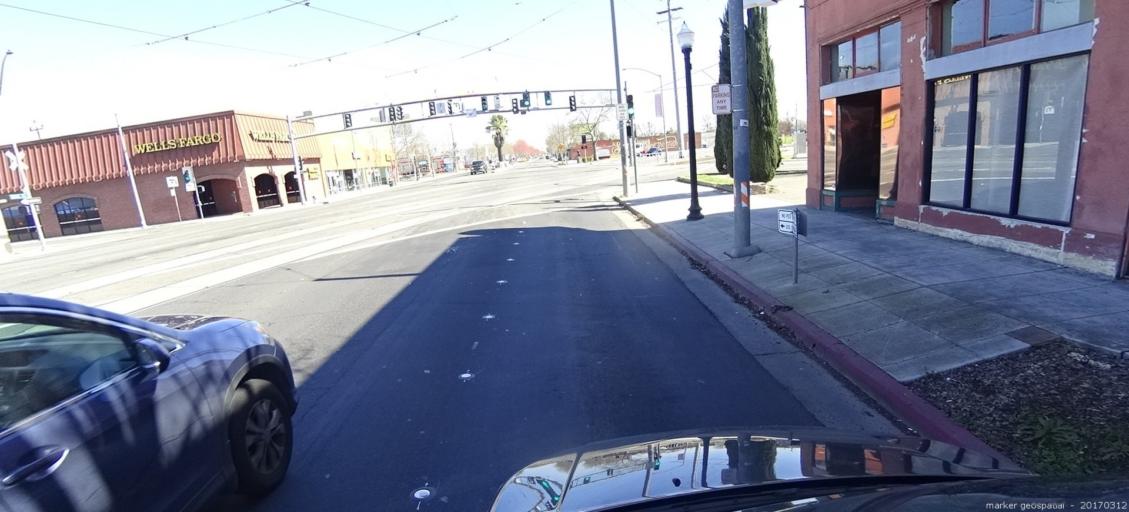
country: US
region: California
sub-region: Sacramento County
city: Sacramento
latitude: 38.6061
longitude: -121.4590
